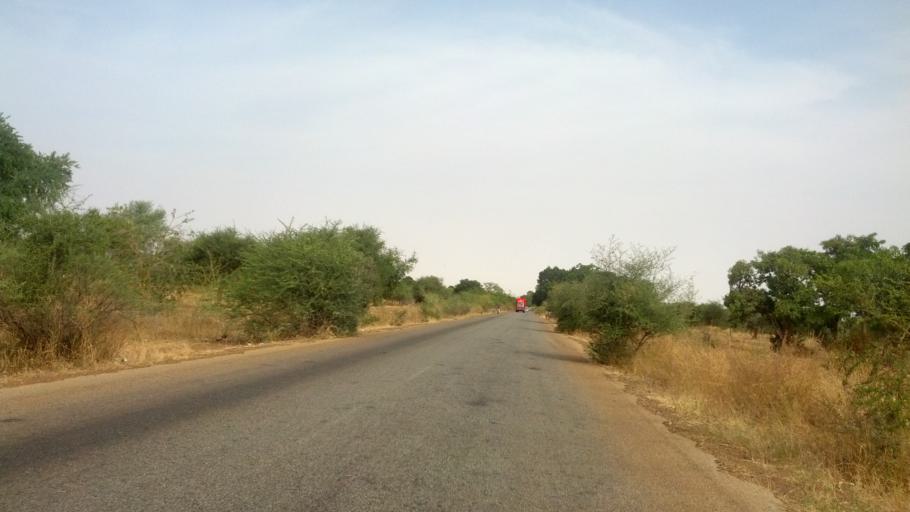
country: BF
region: Centre-Nord
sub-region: Province du Sanmatenga
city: Kaya
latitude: 12.9747
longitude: -1.0883
